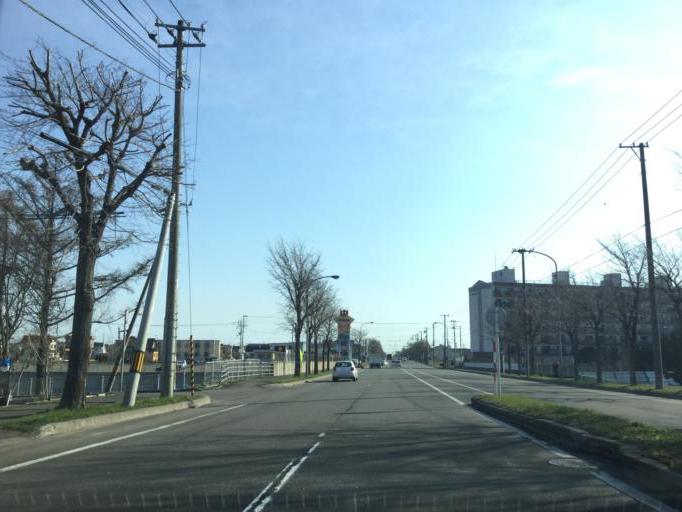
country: JP
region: Hokkaido
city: Ebetsu
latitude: 43.0899
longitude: 141.5061
